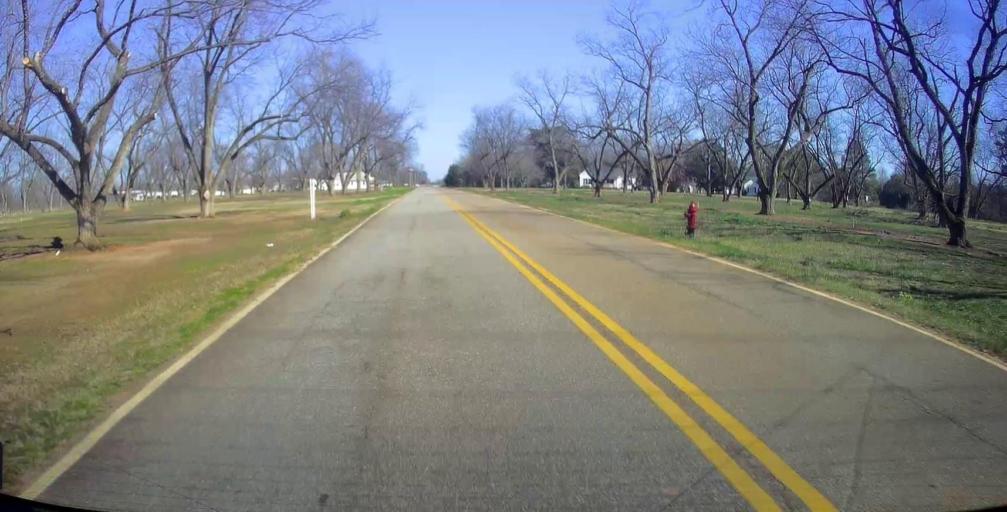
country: US
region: Georgia
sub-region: Peach County
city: Fort Valley
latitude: 32.6119
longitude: -83.9745
